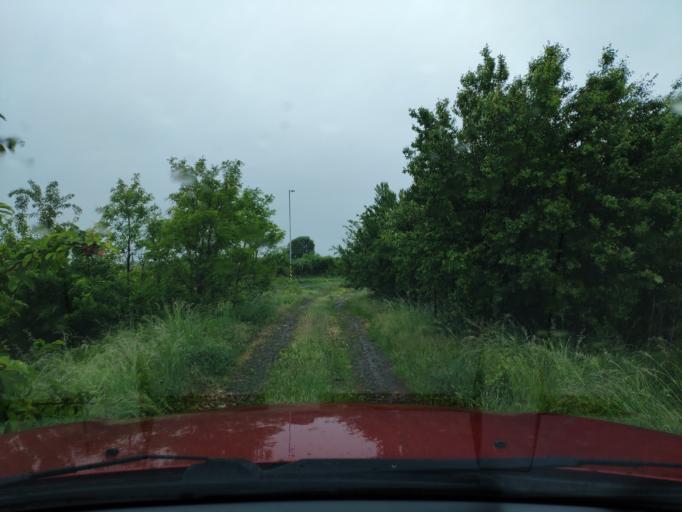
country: SK
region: Kosicky
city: Cierna nad Tisou
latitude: 48.4170
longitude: 22.0335
